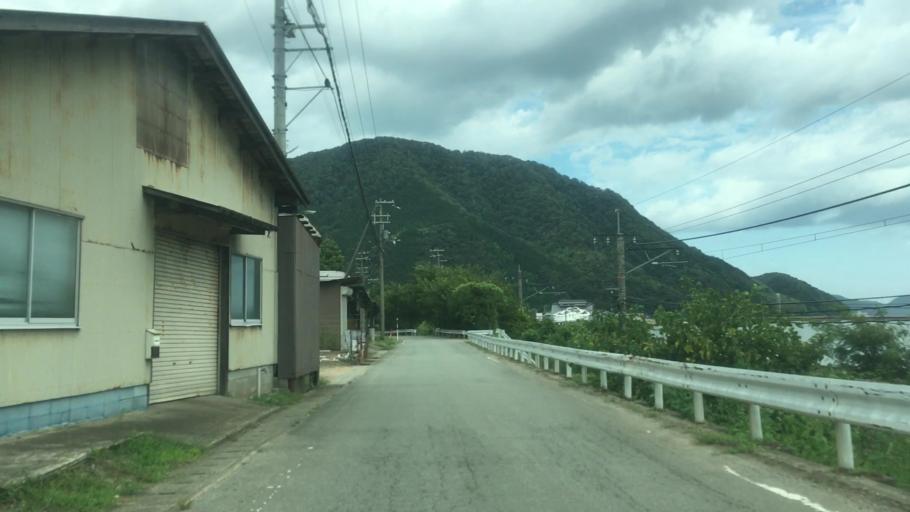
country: JP
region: Hyogo
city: Toyooka
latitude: 35.6004
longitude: 134.8014
